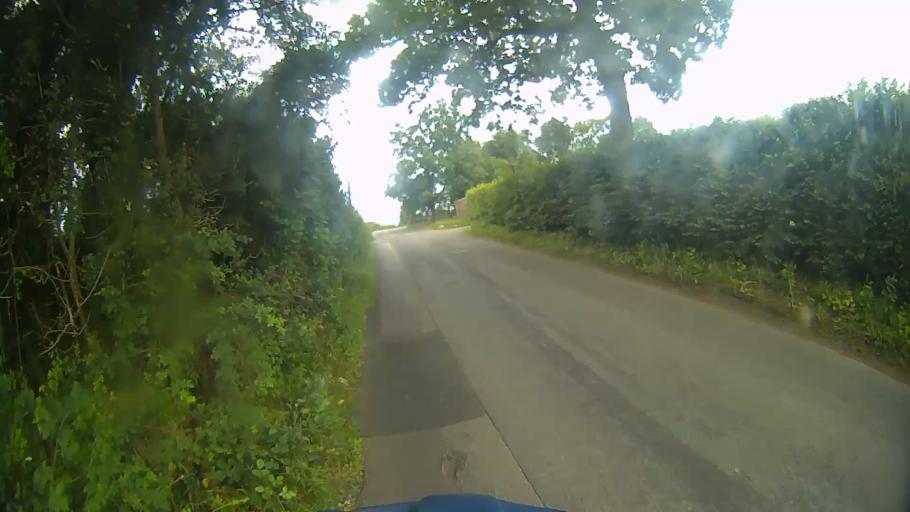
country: GB
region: England
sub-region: Hampshire
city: Kingsley
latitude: 51.1789
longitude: -0.8719
